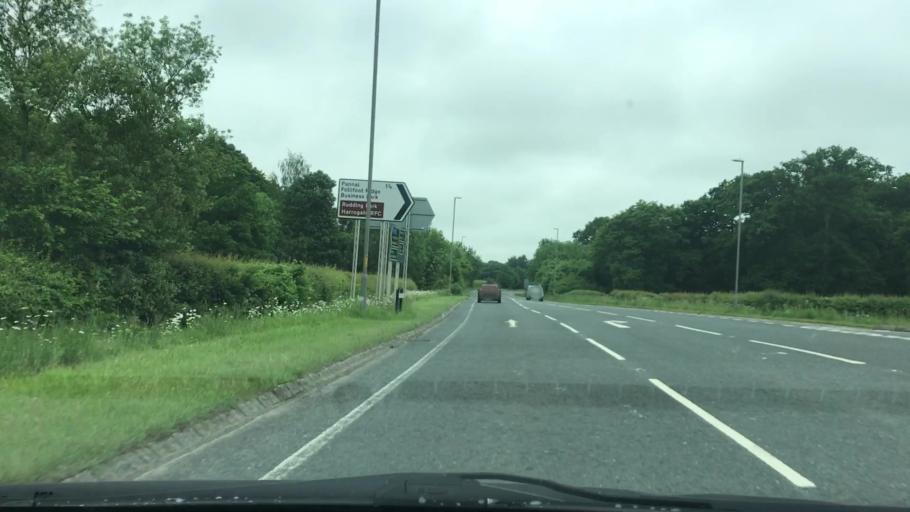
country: GB
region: England
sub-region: North Yorkshire
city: Pannal
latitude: 53.9656
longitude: -1.4965
